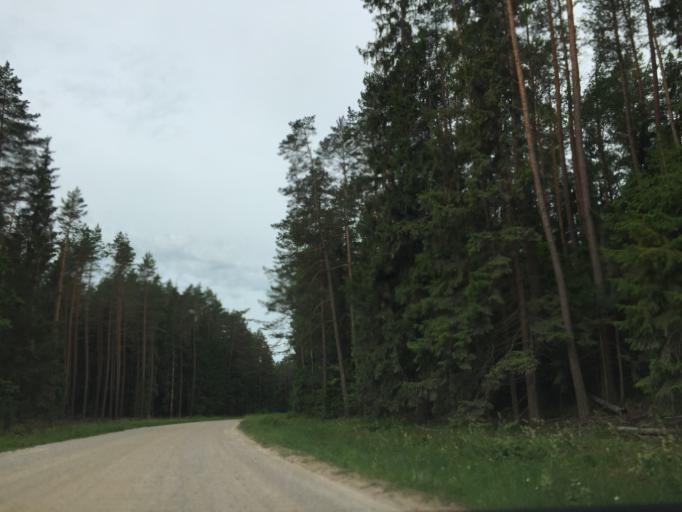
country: LV
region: Tukuma Rajons
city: Tukums
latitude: 57.0027
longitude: 23.1535
